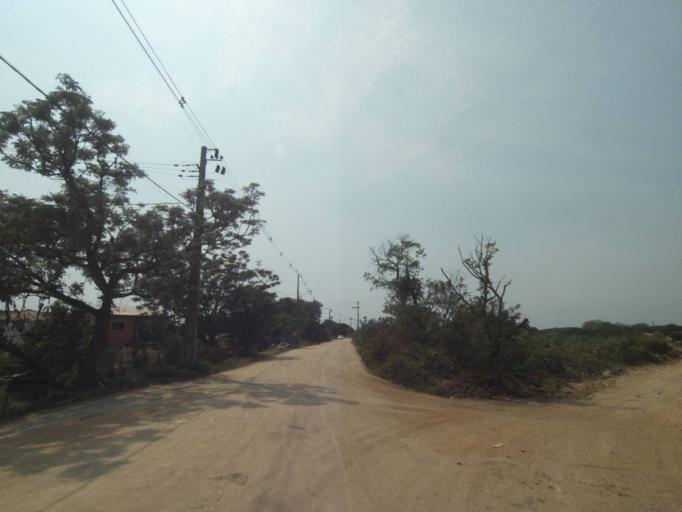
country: BR
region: Parana
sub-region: Sao Jose Dos Pinhais
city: Sao Jose dos Pinhais
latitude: -25.4987
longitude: -49.2031
